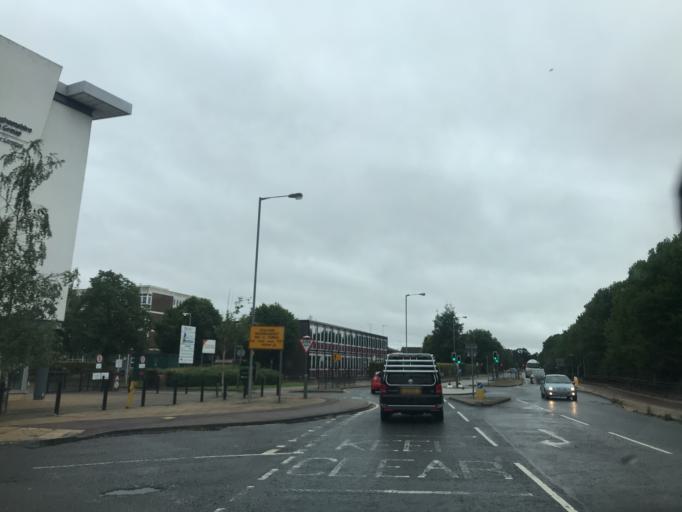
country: GB
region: England
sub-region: Buckinghamshire
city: Aylesbury
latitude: 51.8144
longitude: -0.8234
